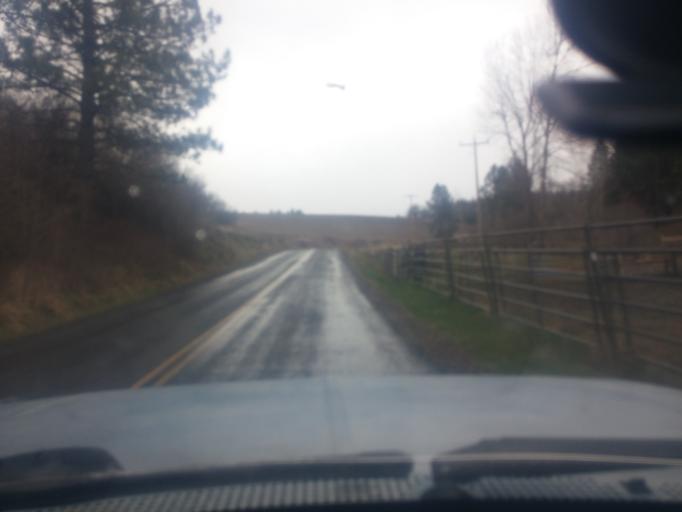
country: US
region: Idaho
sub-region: Latah County
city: Moscow
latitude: 46.9197
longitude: -116.9217
